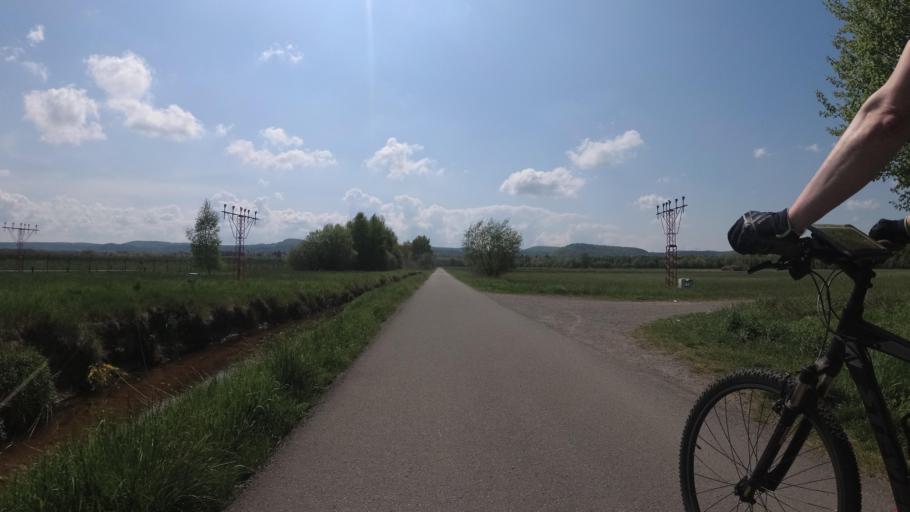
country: DE
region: Rheinland-Pfalz
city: Ramstein-Miesenbach
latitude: 49.4357
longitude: 7.5671
